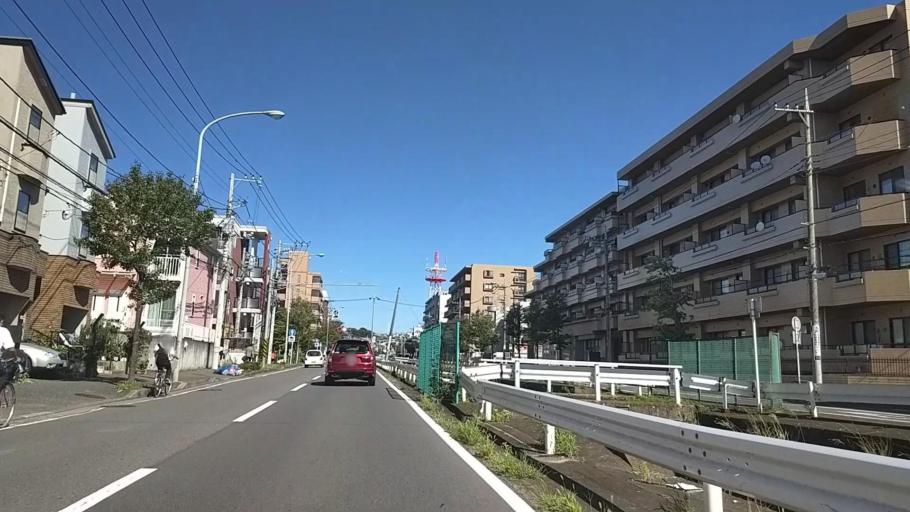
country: JP
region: Tokyo
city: Chofugaoka
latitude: 35.5751
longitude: 139.5492
